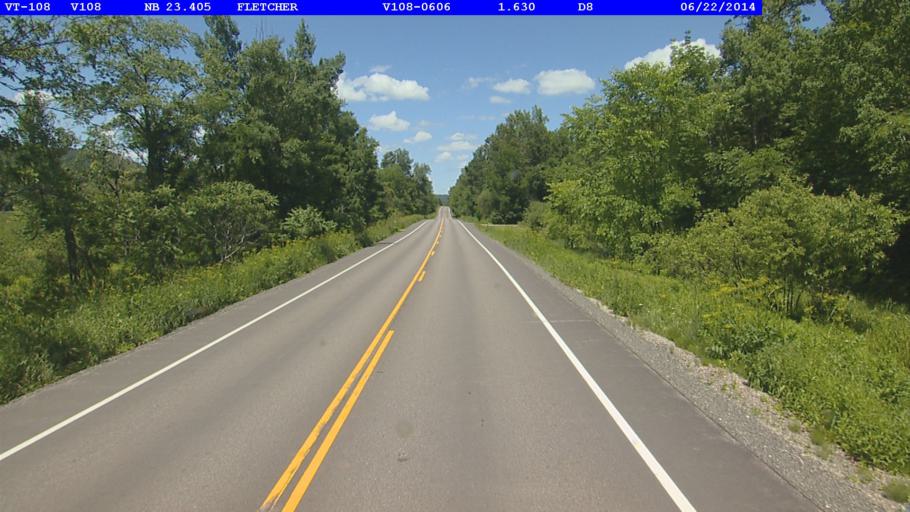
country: US
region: Vermont
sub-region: Lamoille County
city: Johnson
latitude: 44.7237
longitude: -72.8299
